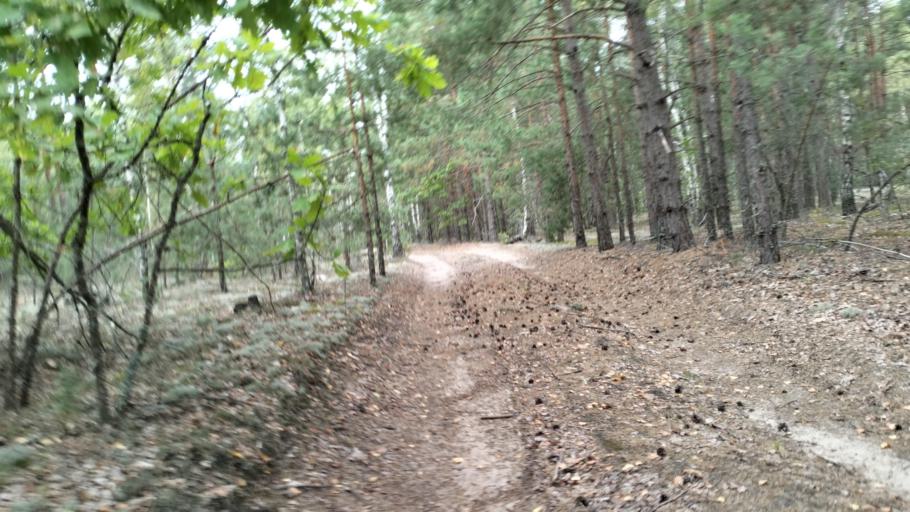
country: BY
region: Brest
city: Davyd-Haradok
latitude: 51.8784
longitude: 27.2173
